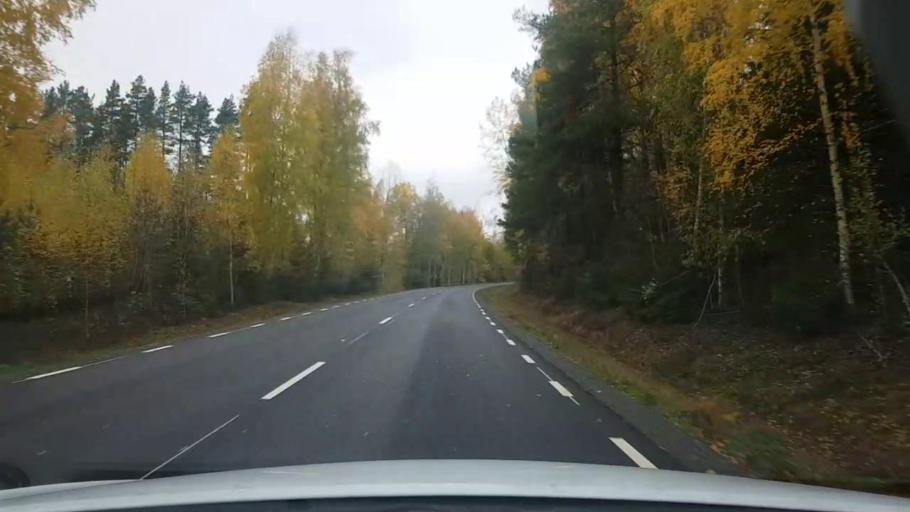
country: SE
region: OErebro
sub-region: Laxa Kommun
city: Laxa
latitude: 58.8215
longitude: 14.5482
